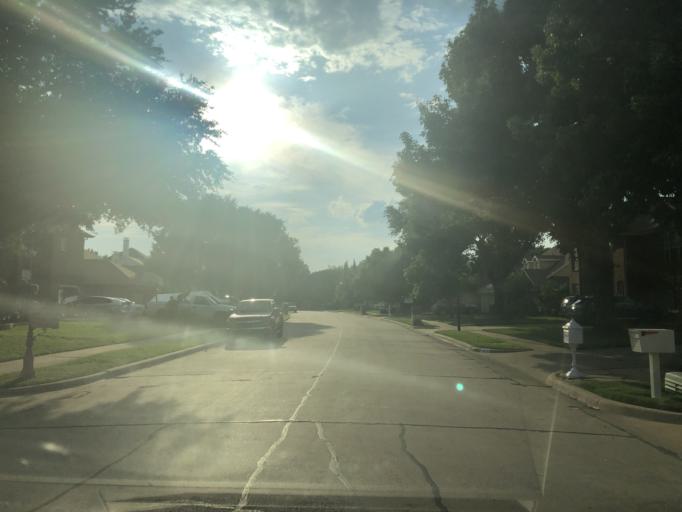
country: US
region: Texas
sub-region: Dallas County
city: Irving
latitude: 32.7896
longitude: -96.9658
